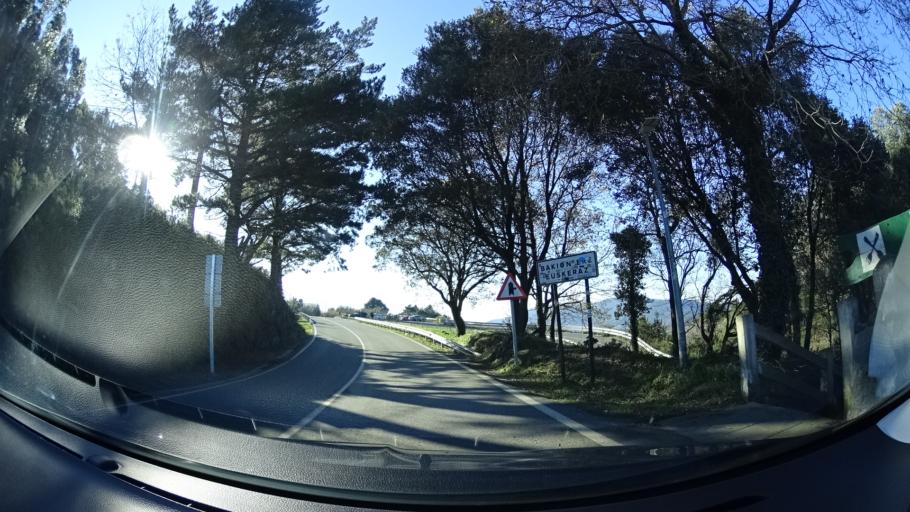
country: ES
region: Basque Country
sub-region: Bizkaia
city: Bakio
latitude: 43.4401
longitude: -2.7827
